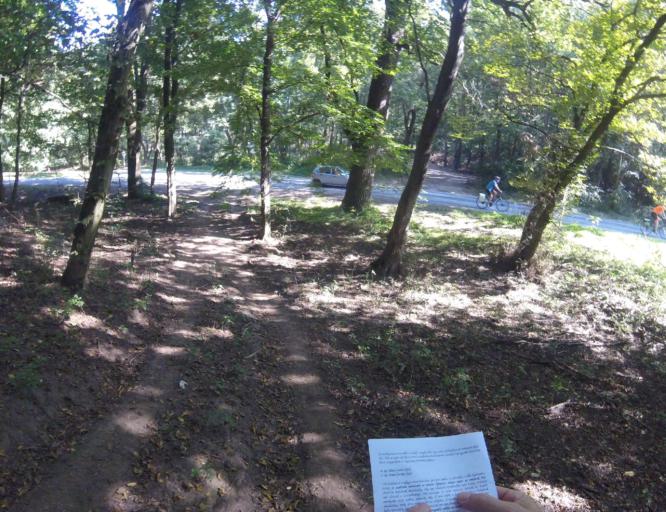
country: HU
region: Fejer
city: Lovasbereny
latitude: 47.2750
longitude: 18.5928
